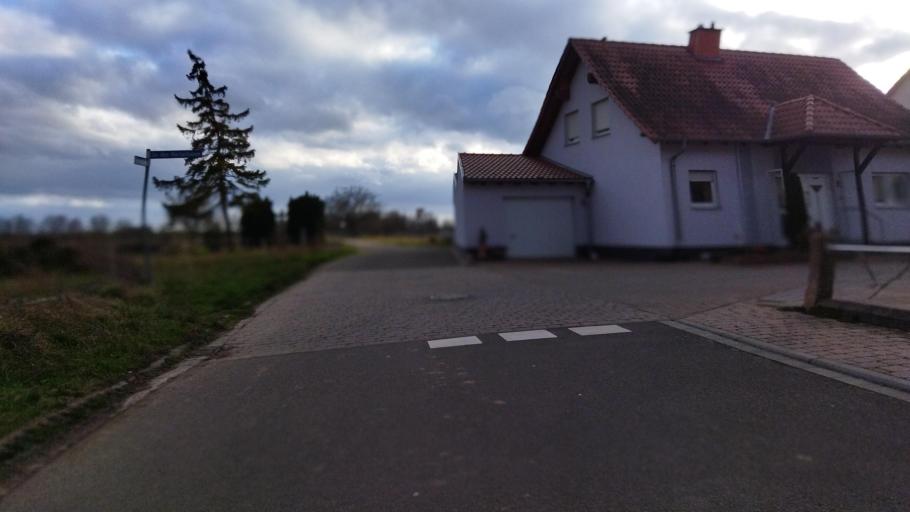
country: DE
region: Rheinland-Pfalz
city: Niederkirchen bei Deidesheim
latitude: 49.4080
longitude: 8.2161
